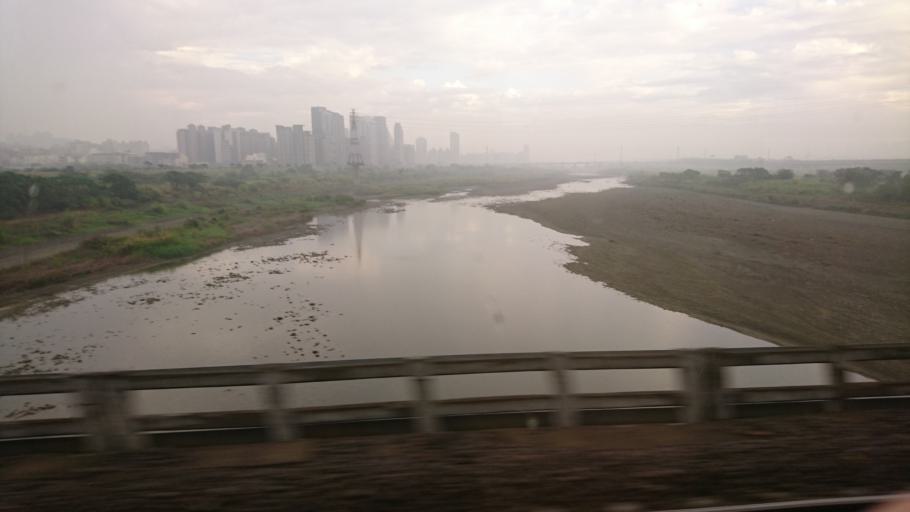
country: TW
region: Taiwan
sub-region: Hsinchu
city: Zhubei
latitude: 24.8224
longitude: 120.9986
